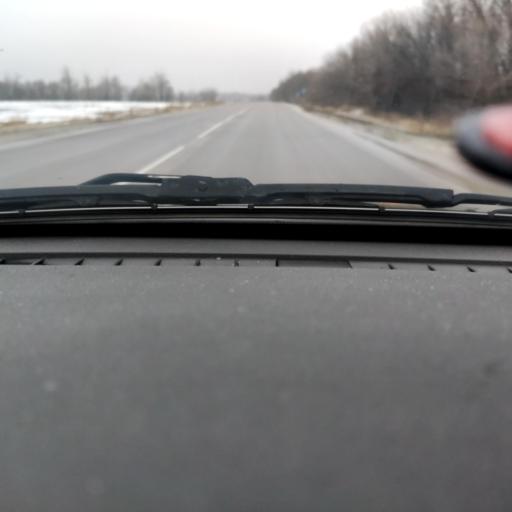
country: RU
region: Voronezj
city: Novaya Usman'
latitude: 51.5895
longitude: 39.3411
